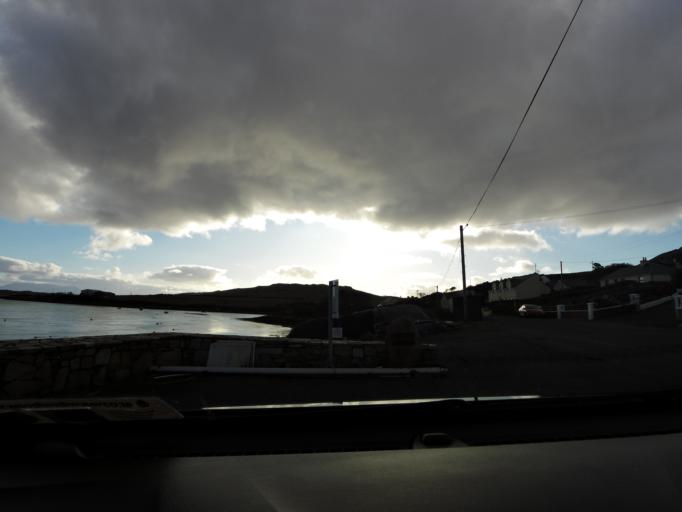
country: IE
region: Connaught
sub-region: Maigh Eo
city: Belmullet
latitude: 53.8801
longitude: -9.9473
